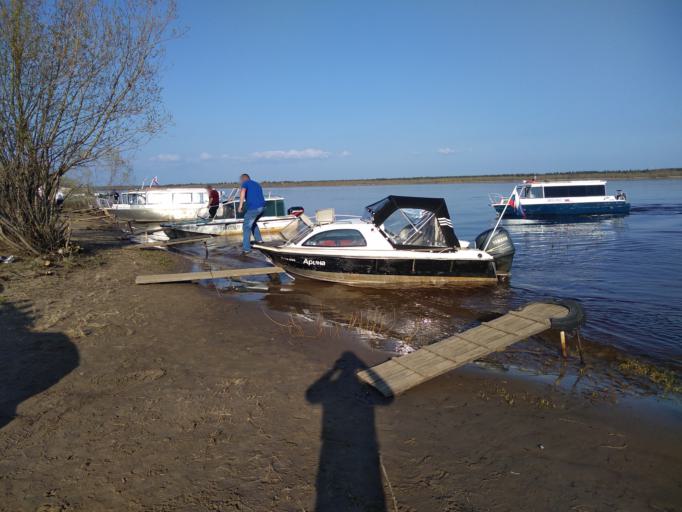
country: RU
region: Komi Republic
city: Pechora
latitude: 65.1055
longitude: 57.1555
